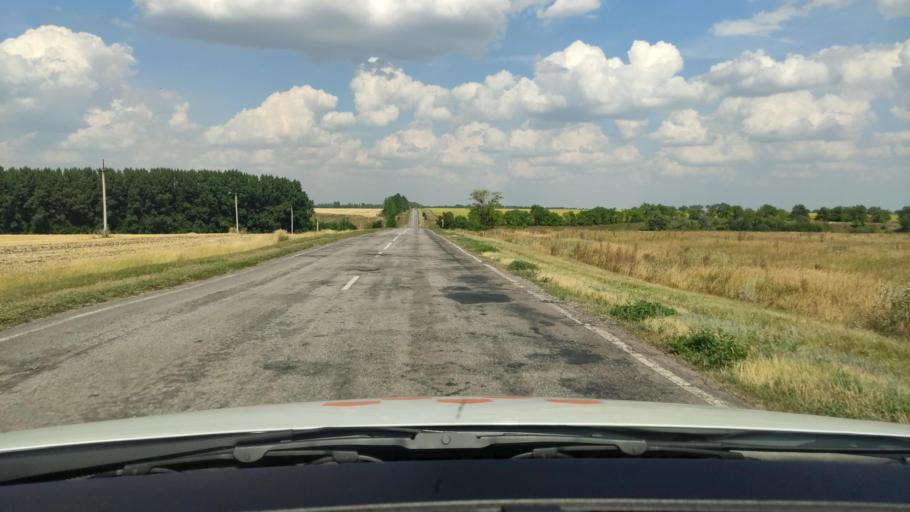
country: RU
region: Voronezj
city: Pereleshinskiy
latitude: 51.7441
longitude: 40.4034
